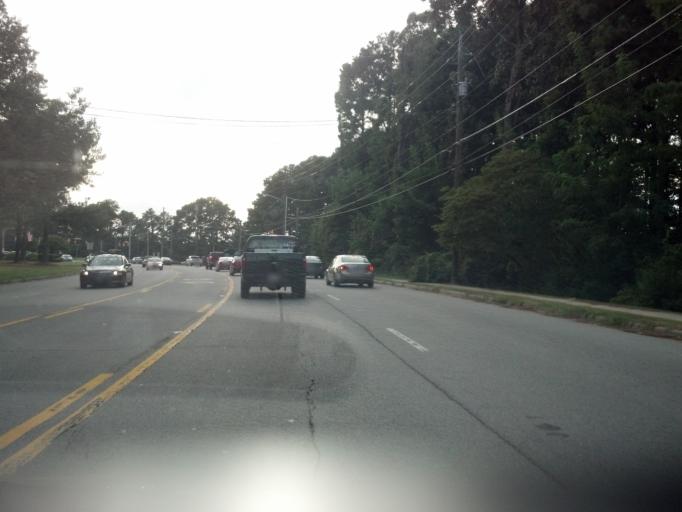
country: US
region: North Carolina
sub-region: Pitt County
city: Greenville
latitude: 35.5906
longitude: -77.3651
